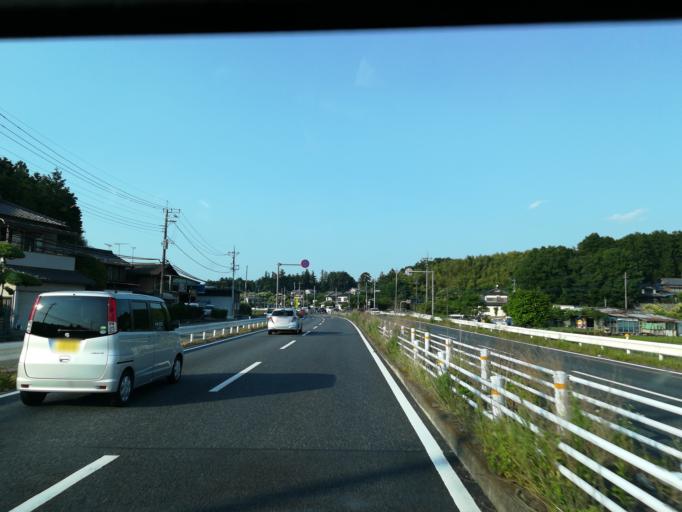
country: JP
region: Saitama
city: Kumagaya
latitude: 36.0845
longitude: 139.3592
